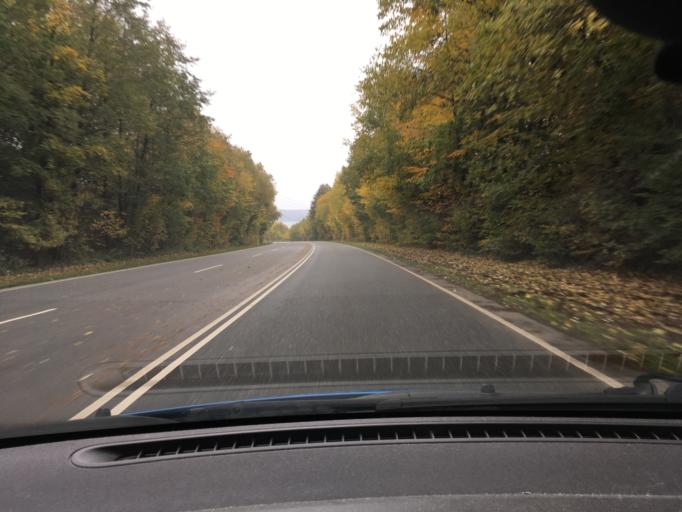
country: DK
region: South Denmark
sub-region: Aabenraa Kommune
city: Aabenraa
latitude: 55.0131
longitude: 9.4238
